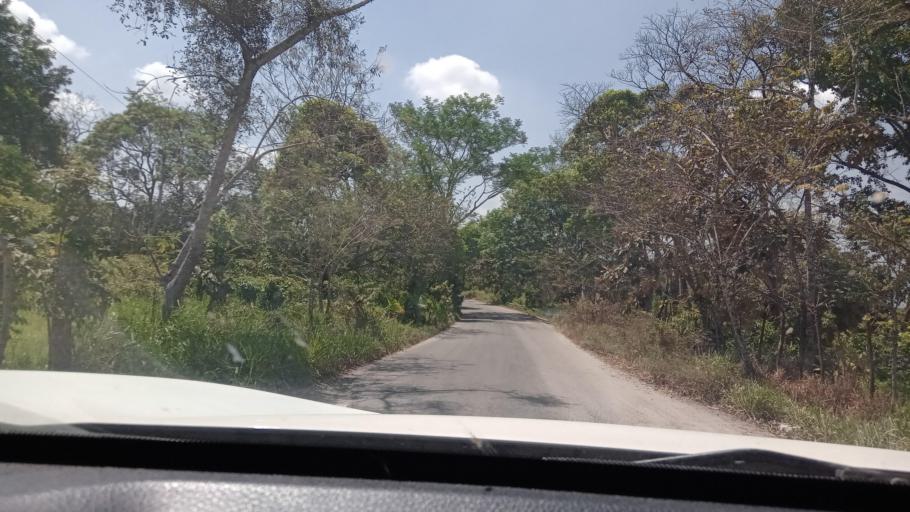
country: MX
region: Veracruz
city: Las Choapas
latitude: 17.7500
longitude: -94.1109
